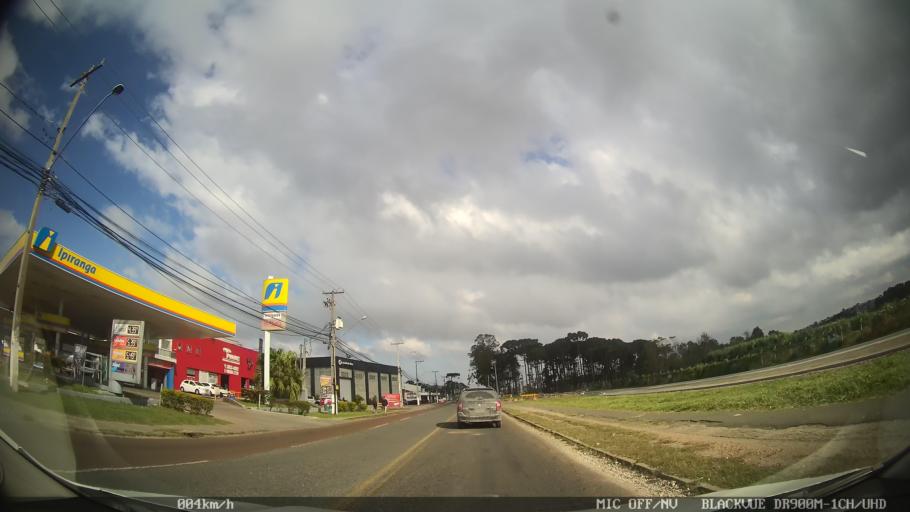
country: BR
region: Parana
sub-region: Pinhais
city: Pinhais
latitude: -25.4105
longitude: -49.1897
